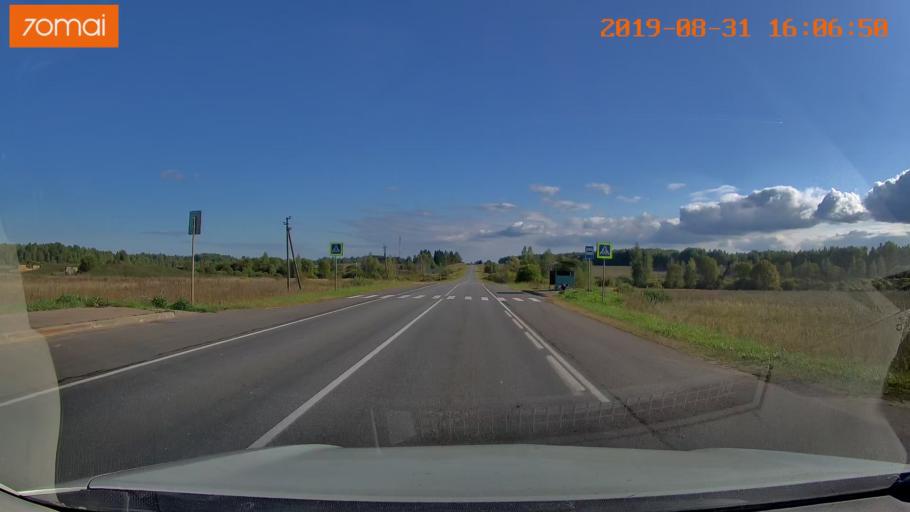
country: RU
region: Kaluga
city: Yukhnov
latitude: 54.6197
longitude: 35.3500
